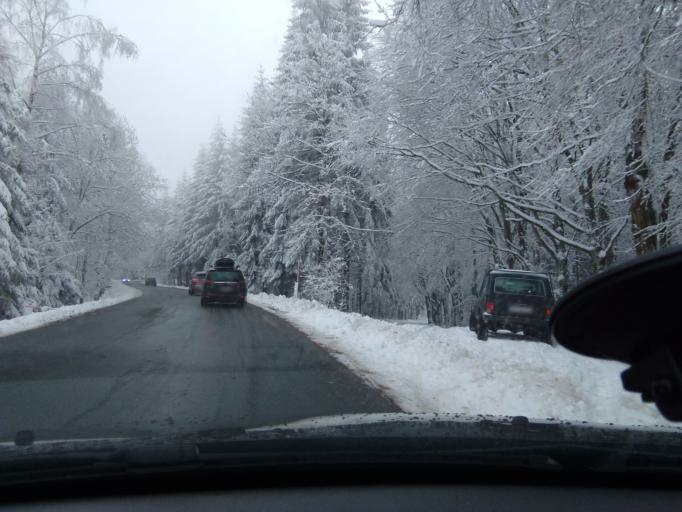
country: DE
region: Saxony
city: Markersbach
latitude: 50.5144
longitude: 12.8571
